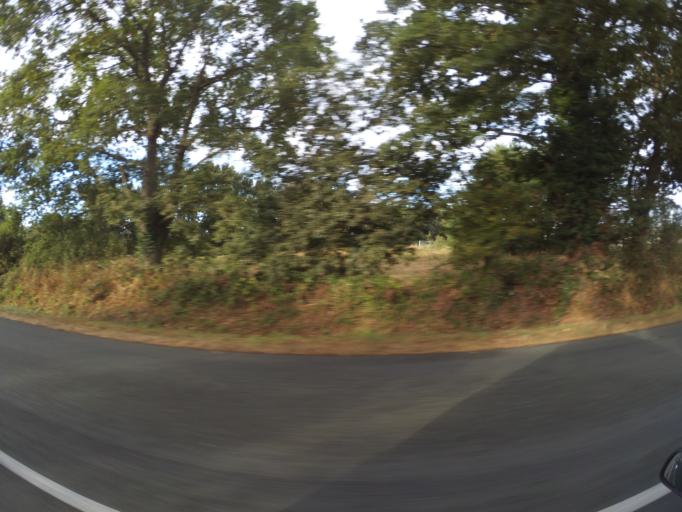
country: FR
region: Pays de la Loire
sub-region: Departement de la Loire-Atlantique
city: La Planche
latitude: 46.9979
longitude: -1.4646
